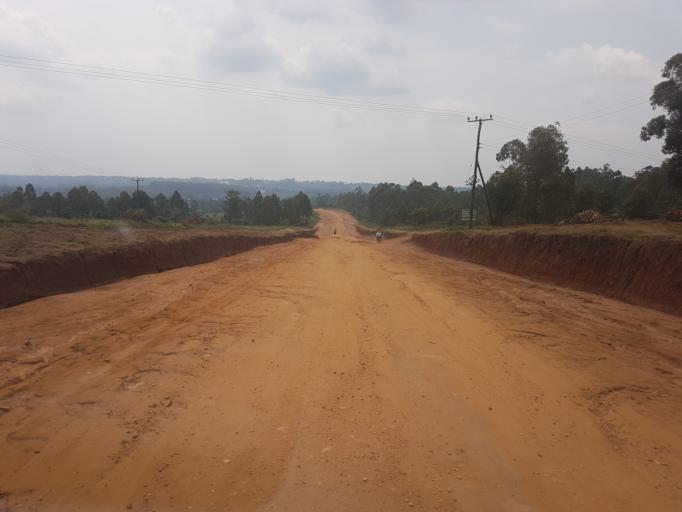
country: UG
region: Western Region
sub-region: Kanungu District
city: Ntungamo
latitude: -0.8139
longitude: 29.7065
